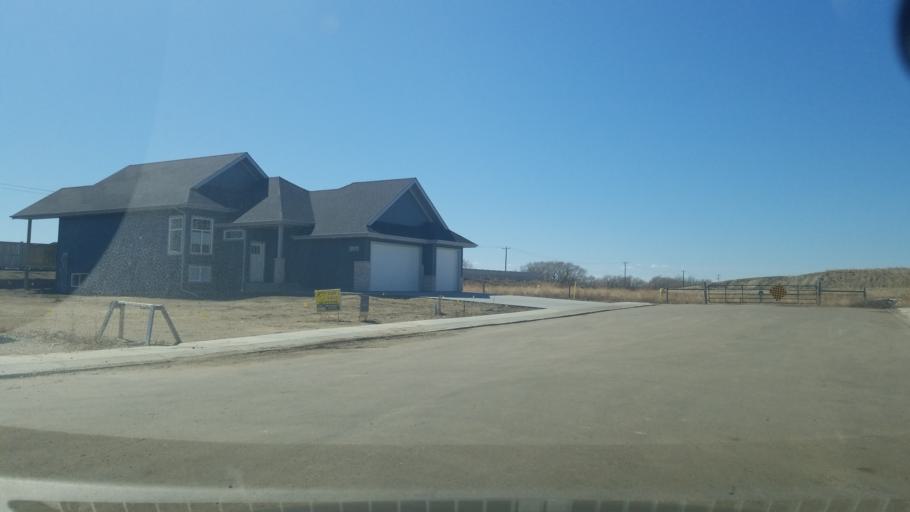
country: CA
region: Saskatchewan
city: Lloydminster
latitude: 53.2496
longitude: -110.0200
